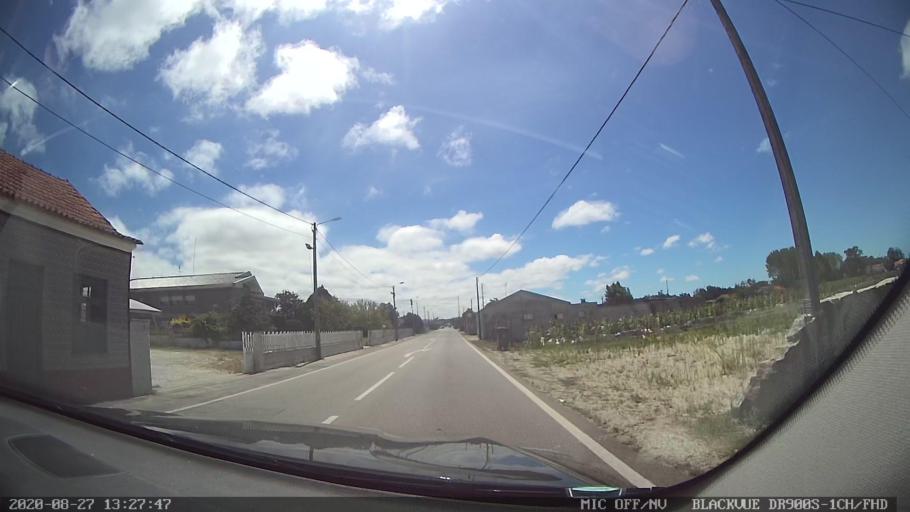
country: PT
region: Aveiro
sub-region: Vagos
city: Vagos
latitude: 40.5271
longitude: -8.6791
